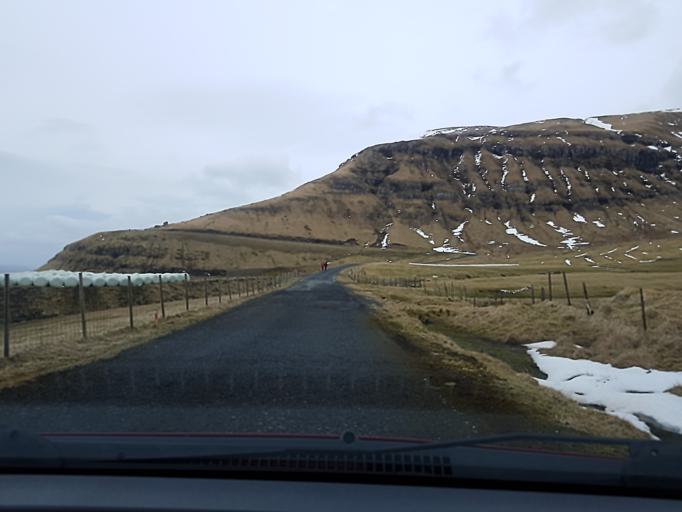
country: FO
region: Streymoy
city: Hoyvik
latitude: 61.9967
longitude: -6.8881
